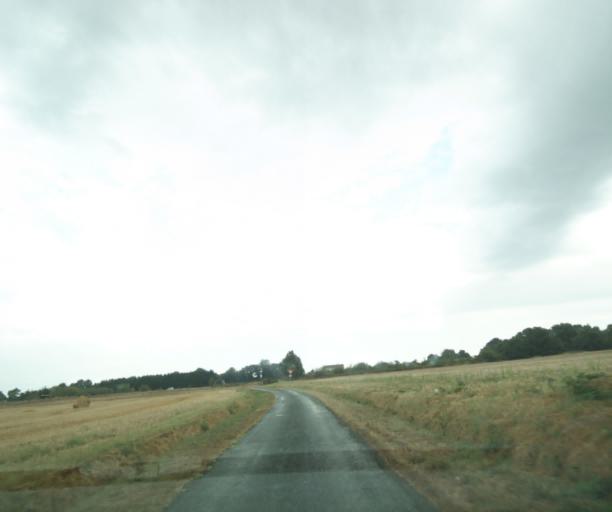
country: FR
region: Poitou-Charentes
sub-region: Departement de la Charente-Maritime
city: Cabariot
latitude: 45.9472
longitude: -0.8690
